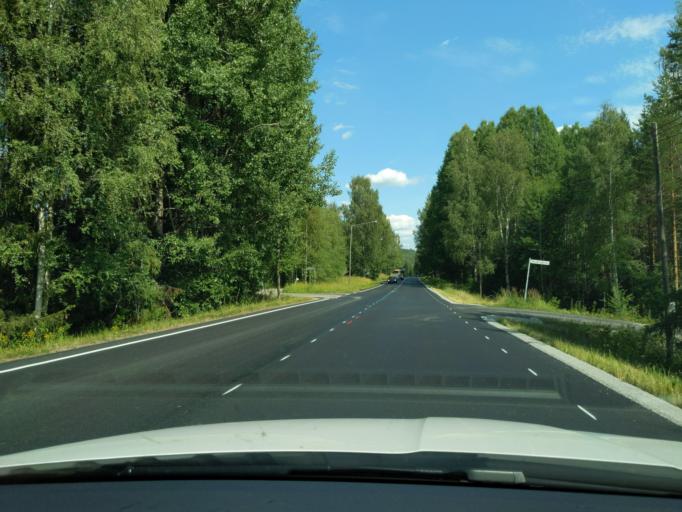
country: FI
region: Paijanne Tavastia
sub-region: Lahti
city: Lahti
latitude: 61.0667
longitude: 25.8083
